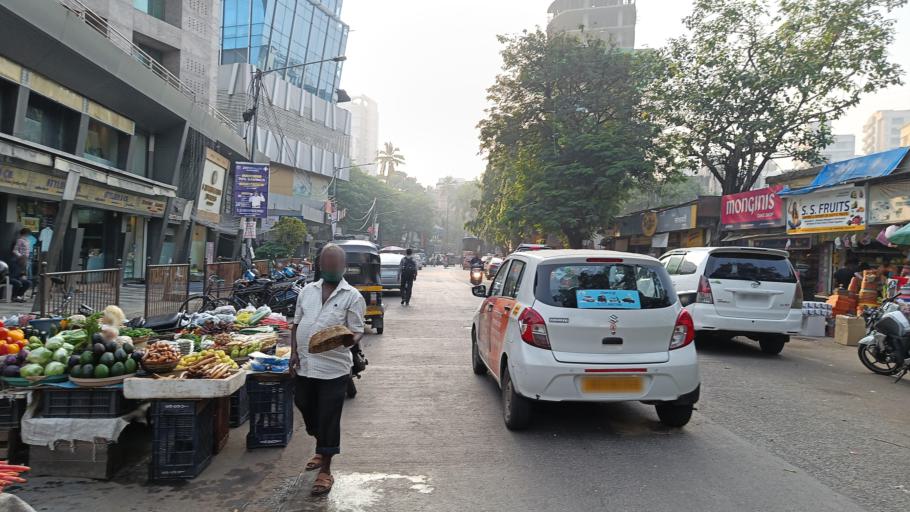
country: IN
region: Maharashtra
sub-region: Mumbai Suburban
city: Mumbai
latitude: 19.0701
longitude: 72.8389
